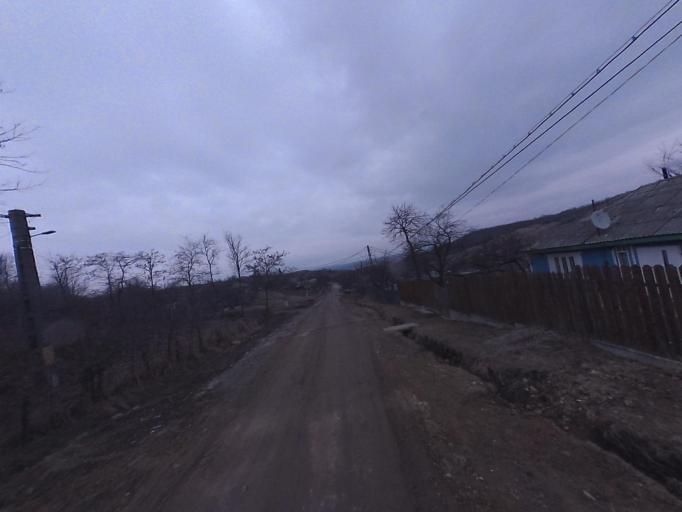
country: RO
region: Iasi
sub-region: Comuna Popricani
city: Popricani
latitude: 47.2923
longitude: 27.5100
